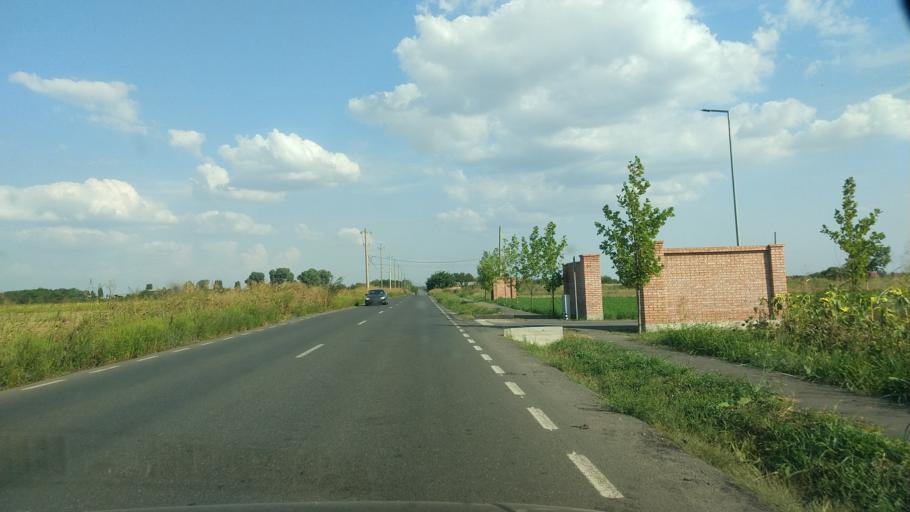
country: RO
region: Ilfov
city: Stefanestii de Jos
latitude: 44.5368
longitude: 26.2228
